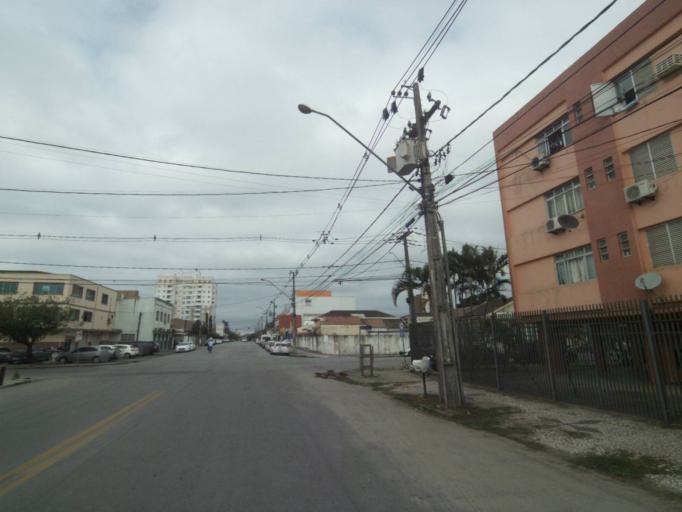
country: BR
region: Parana
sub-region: Paranagua
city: Paranagua
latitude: -25.5138
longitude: -48.5114
